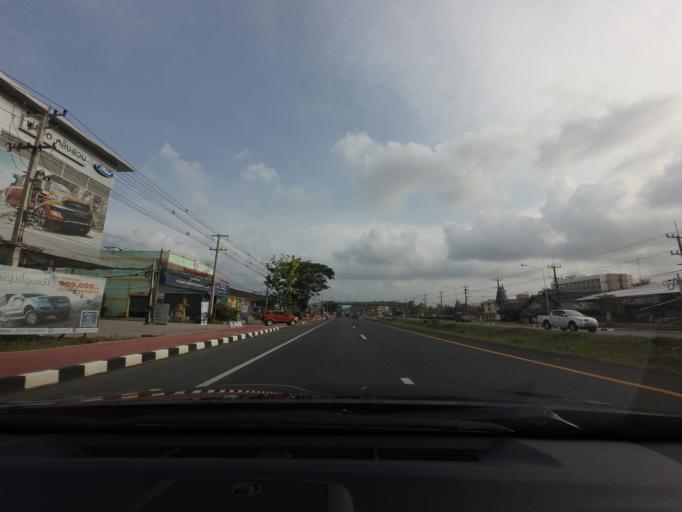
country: TH
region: Chumphon
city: Lang Suan
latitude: 9.9847
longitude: 99.0679
